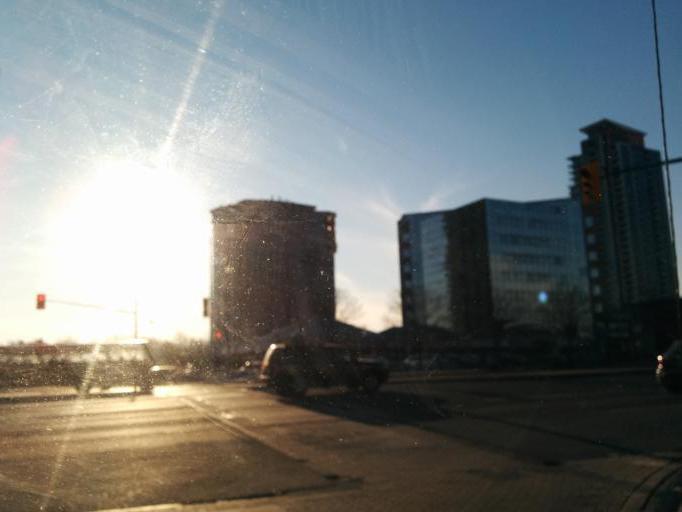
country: CA
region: Ontario
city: Mississauga
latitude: 43.6058
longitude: -79.6511
